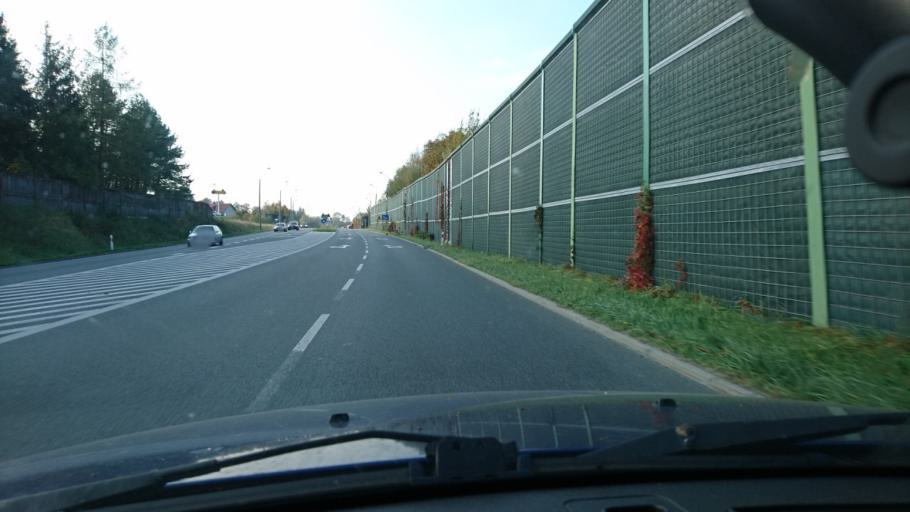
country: PL
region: Silesian Voivodeship
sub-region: Powiat cieszynski
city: Ustron
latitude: 49.7159
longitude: 18.8038
